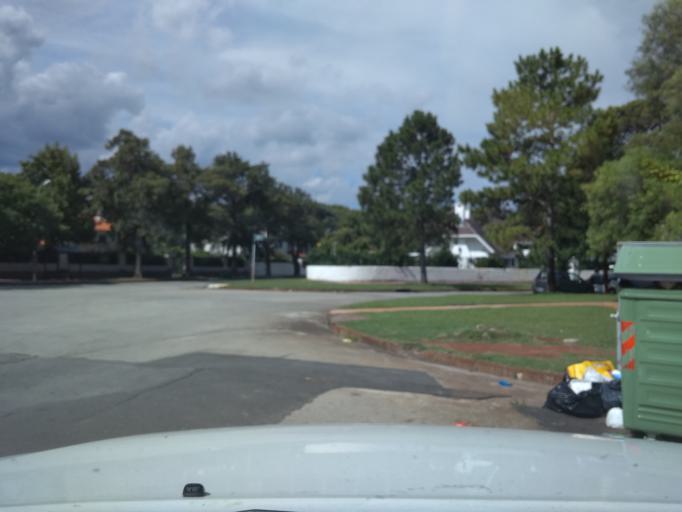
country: UY
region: Canelones
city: Barra de Carrasco
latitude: -34.8888
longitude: -56.0540
